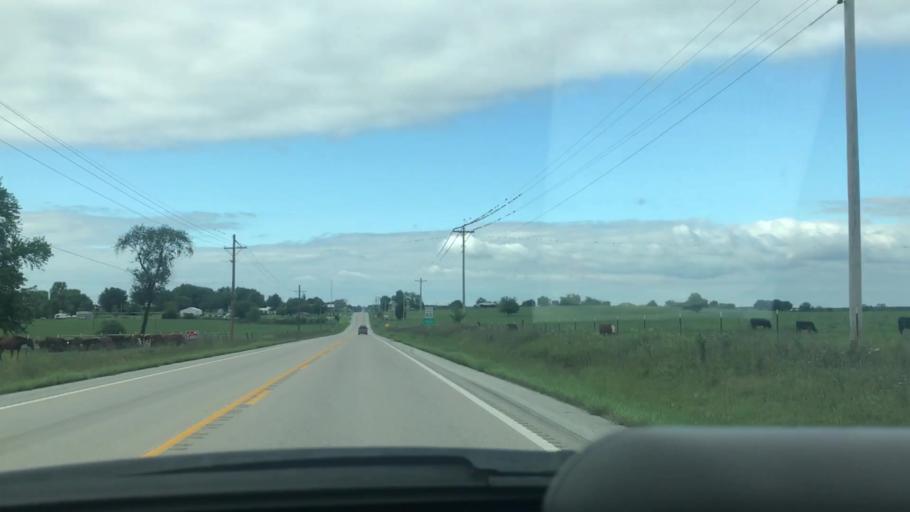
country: US
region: Missouri
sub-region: Hickory County
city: Hermitage
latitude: 37.9328
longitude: -93.2085
